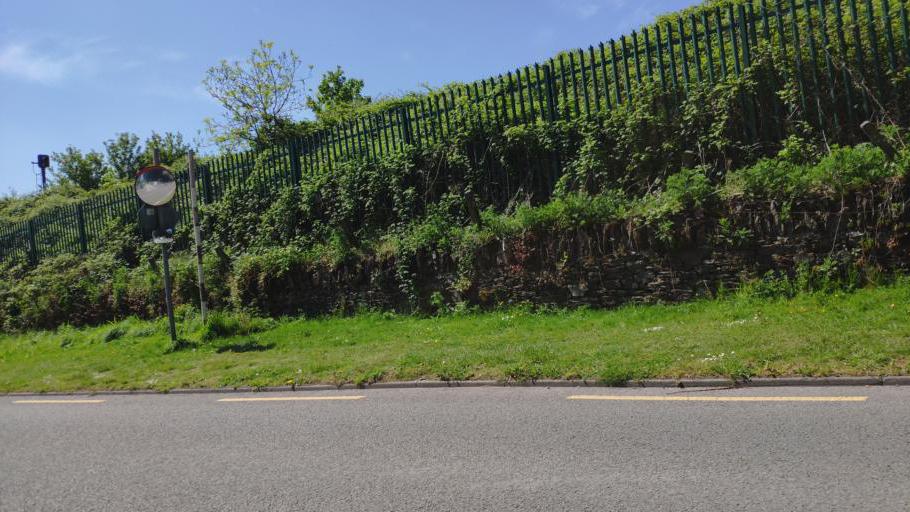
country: IE
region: Munster
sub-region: County Cork
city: Cork
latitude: 51.9288
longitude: -8.4882
